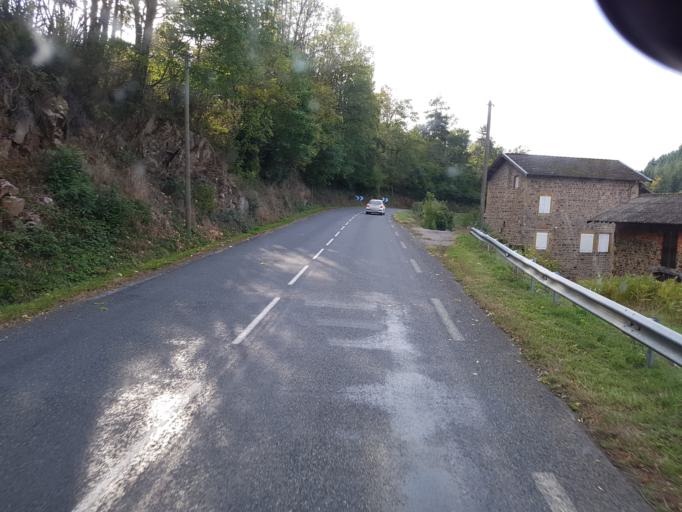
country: FR
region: Bourgogne
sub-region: Departement de Saone-et-Loire
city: Chauffailles
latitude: 46.2200
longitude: 4.4290
